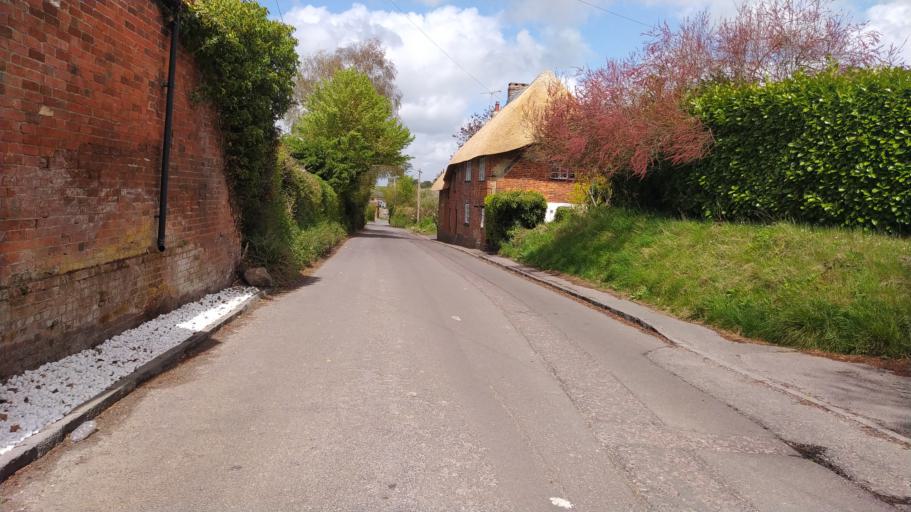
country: GB
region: England
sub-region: Dorset
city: Sturminster Newton
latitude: 50.8983
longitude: -2.2767
